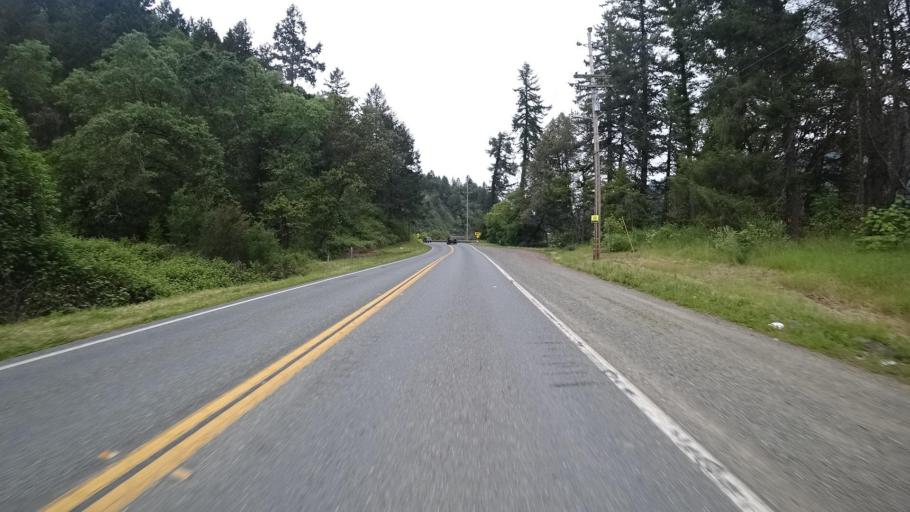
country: US
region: California
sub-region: Humboldt County
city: Willow Creek
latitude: 41.0362
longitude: -123.6693
